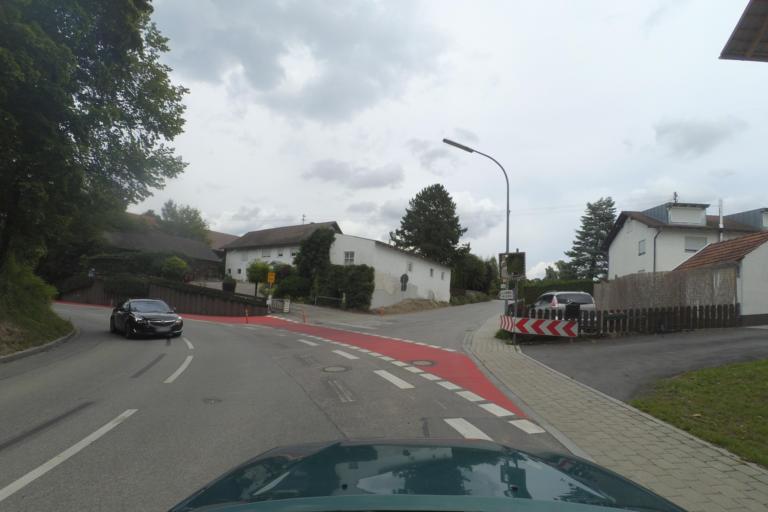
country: DE
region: Bavaria
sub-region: Lower Bavaria
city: Mamming
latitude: 48.6549
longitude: 12.6072
